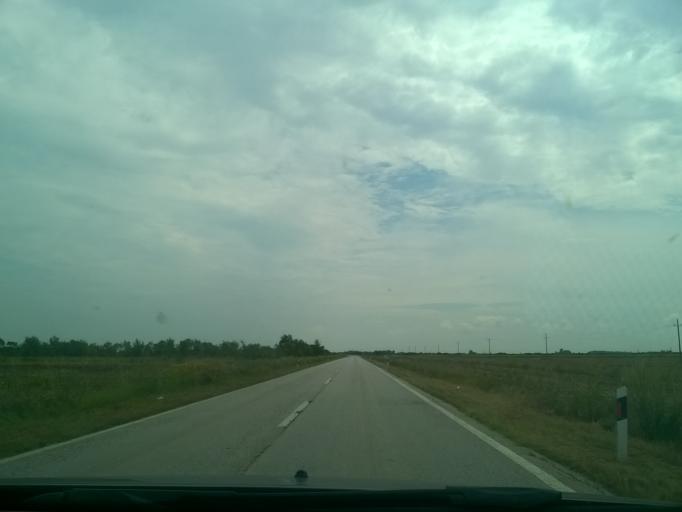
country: RS
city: Konak
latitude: 45.3321
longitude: 20.8754
